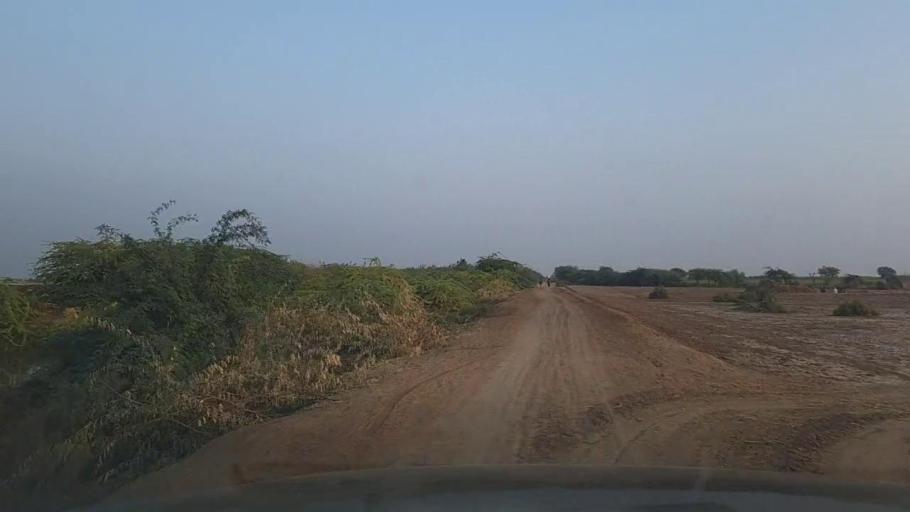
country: PK
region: Sindh
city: Jati
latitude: 24.5397
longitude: 68.4017
